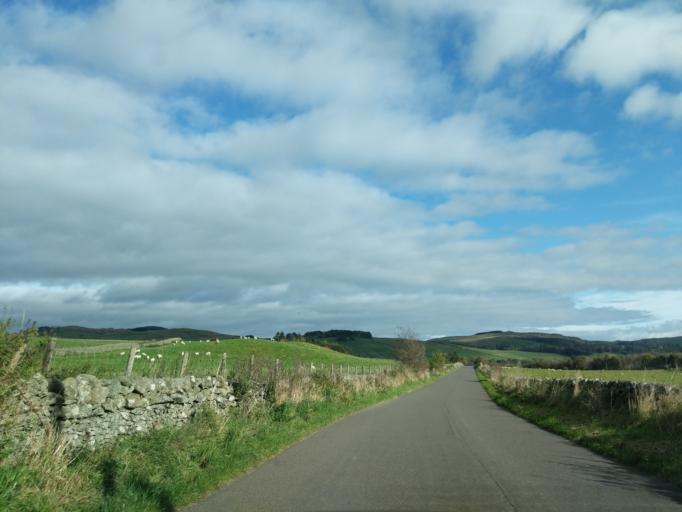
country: GB
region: Scotland
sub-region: Dumfries and Galloway
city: Thornhill
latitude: 55.1890
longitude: -3.9286
